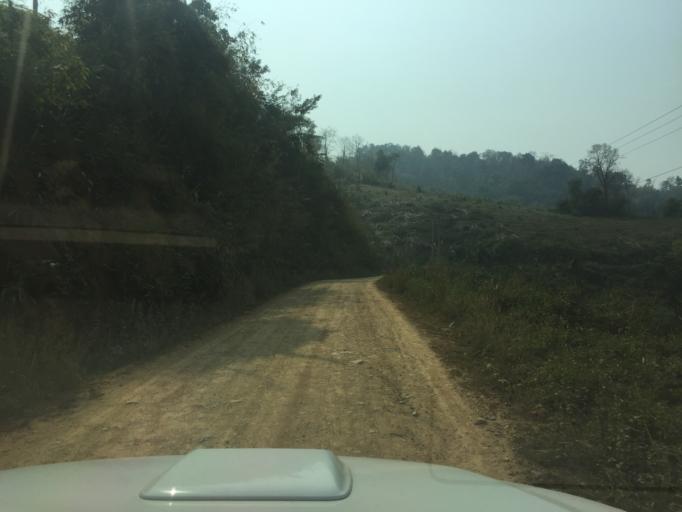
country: TH
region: Phayao
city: Phu Sang
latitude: 19.6239
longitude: 100.5389
